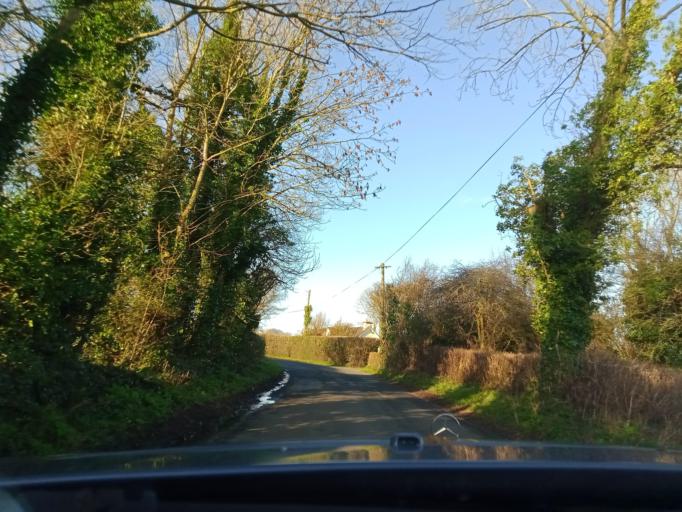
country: IE
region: Leinster
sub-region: Kilkenny
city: Callan
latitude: 52.5014
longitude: -7.3691
